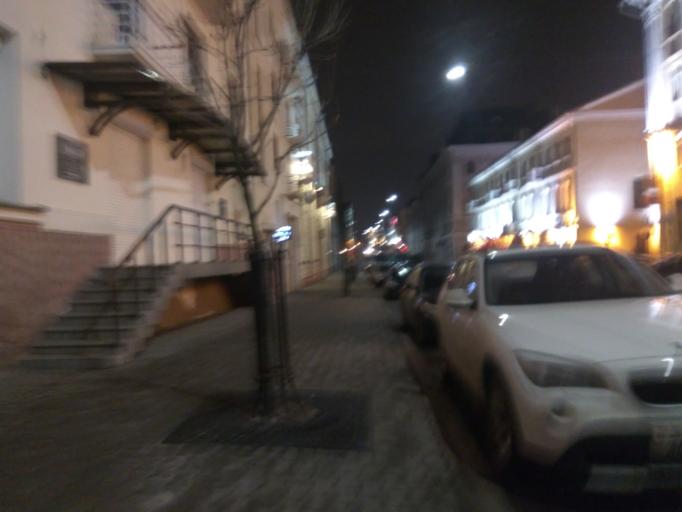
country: BY
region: Minsk
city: Minsk
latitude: 53.8980
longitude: 27.5576
